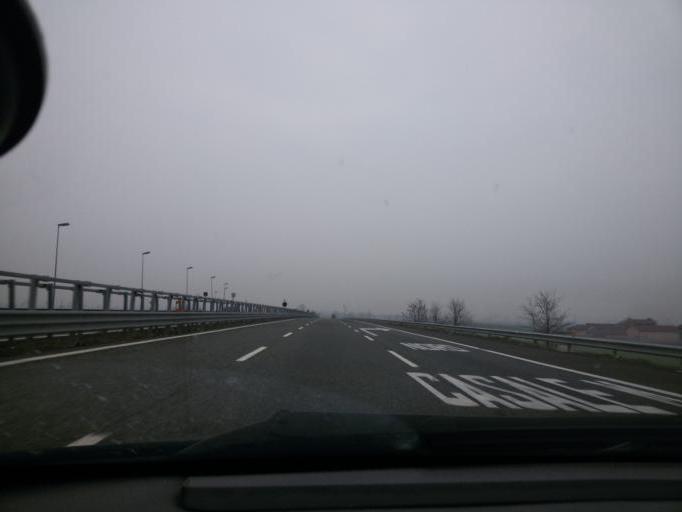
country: IT
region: Piedmont
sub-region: Provincia di Alessandria
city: Villanova Monferrato
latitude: 45.1633
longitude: 8.4878
